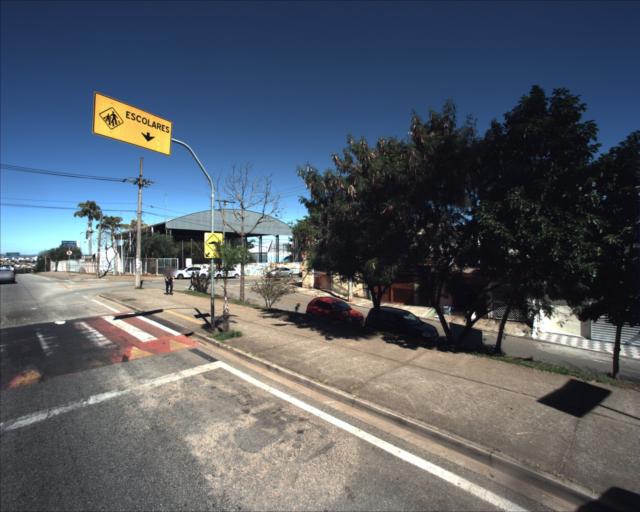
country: BR
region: Sao Paulo
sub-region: Sorocaba
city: Sorocaba
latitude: -23.4981
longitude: -47.5083
